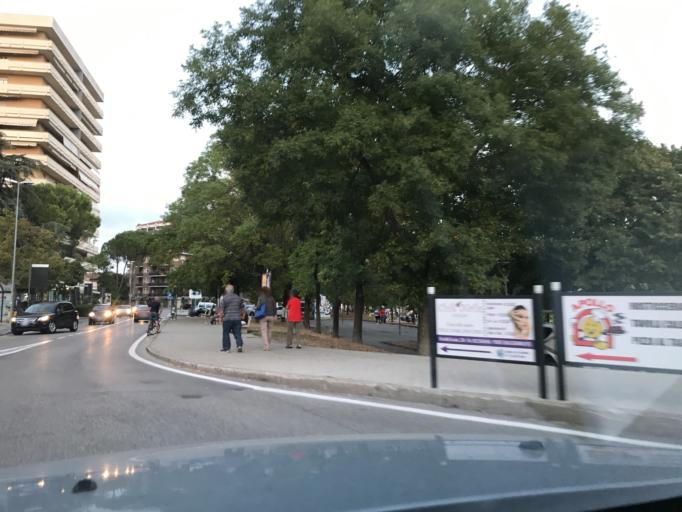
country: IT
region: Umbria
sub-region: Provincia di Perugia
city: Via Lippia
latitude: 43.0893
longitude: 12.4410
